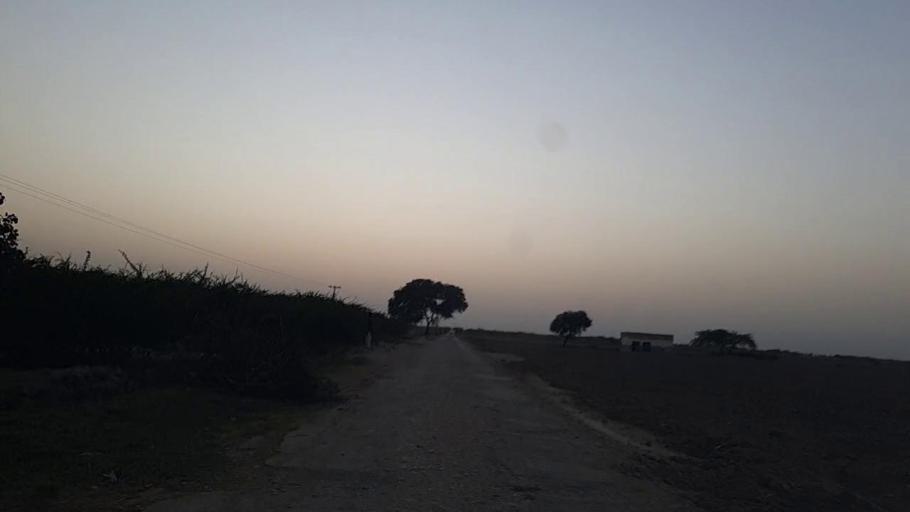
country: PK
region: Sindh
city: Naukot
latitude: 24.7532
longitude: 69.2891
